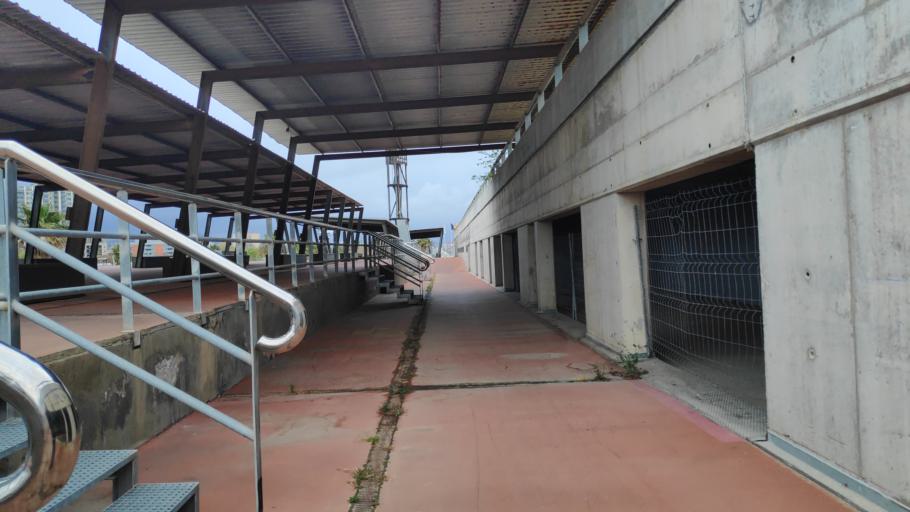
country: ES
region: Catalonia
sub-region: Provincia de Barcelona
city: Sant Adria de Besos
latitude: 41.4147
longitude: 2.2288
